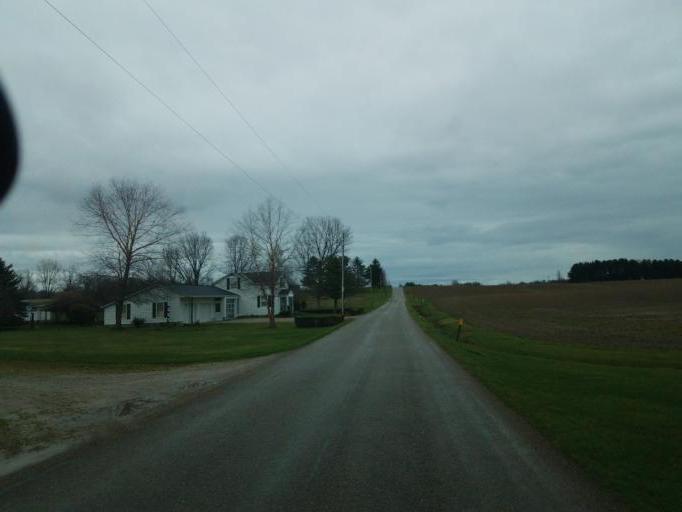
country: US
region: Ohio
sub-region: Richland County
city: Lexington
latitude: 40.6635
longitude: -82.6840
